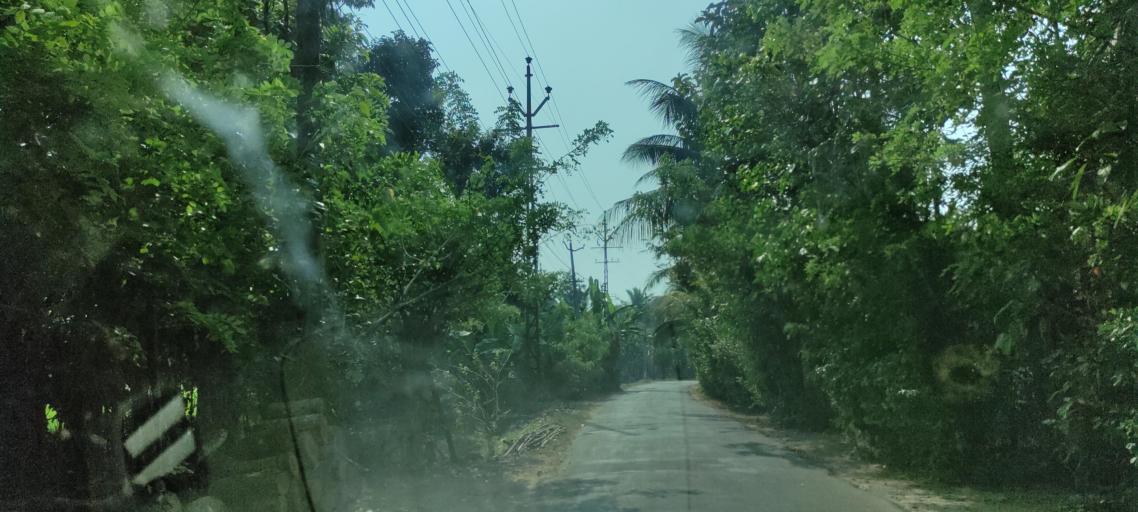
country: IN
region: Kerala
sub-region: Pattanamtitta
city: Tiruvalla
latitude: 9.3603
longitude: 76.5068
